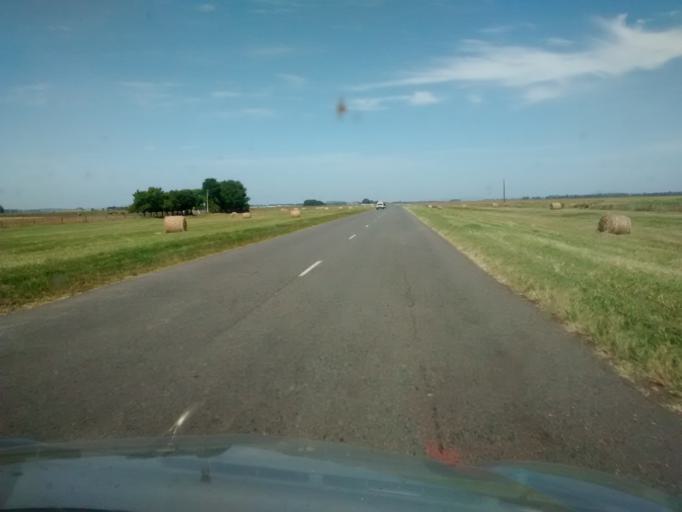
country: AR
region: Buenos Aires
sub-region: Partido de Balcarce
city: Balcarce
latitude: -37.6070
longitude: -58.5011
